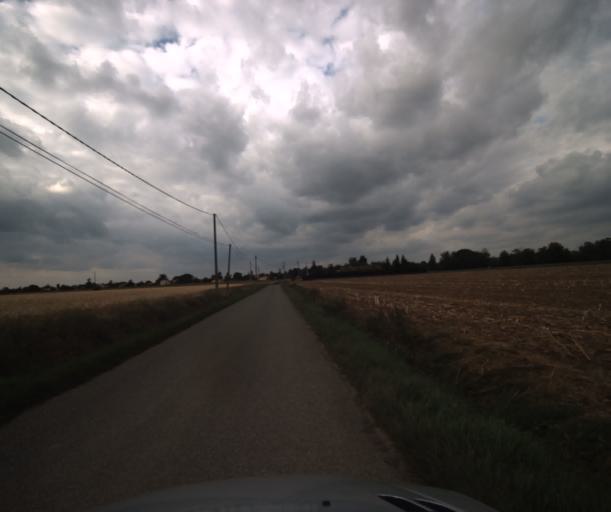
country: FR
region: Midi-Pyrenees
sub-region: Departement de la Haute-Garonne
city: Labarthe-sur-Leze
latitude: 43.4388
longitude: 1.3962
